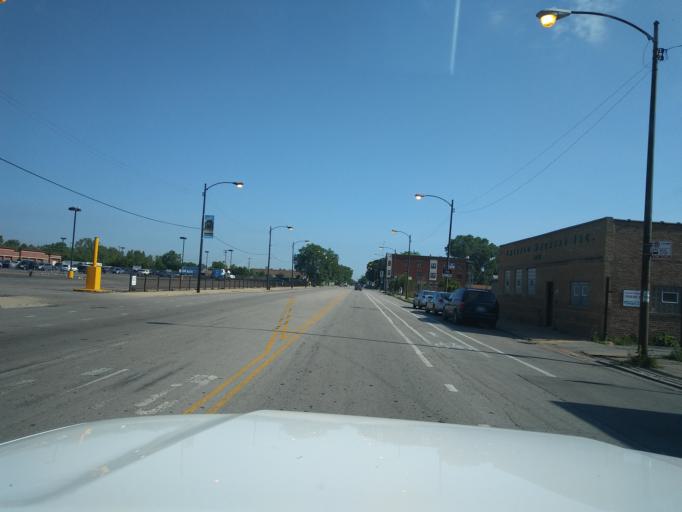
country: US
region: Illinois
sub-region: Cook County
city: Chicago
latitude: 41.8091
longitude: -87.6455
